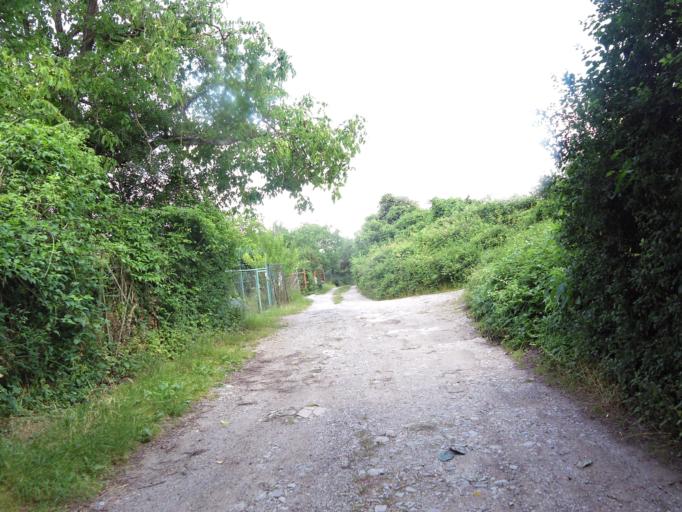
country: DE
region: Bavaria
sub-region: Regierungsbezirk Unterfranken
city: Wuerzburg
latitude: 49.8120
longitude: 9.9279
